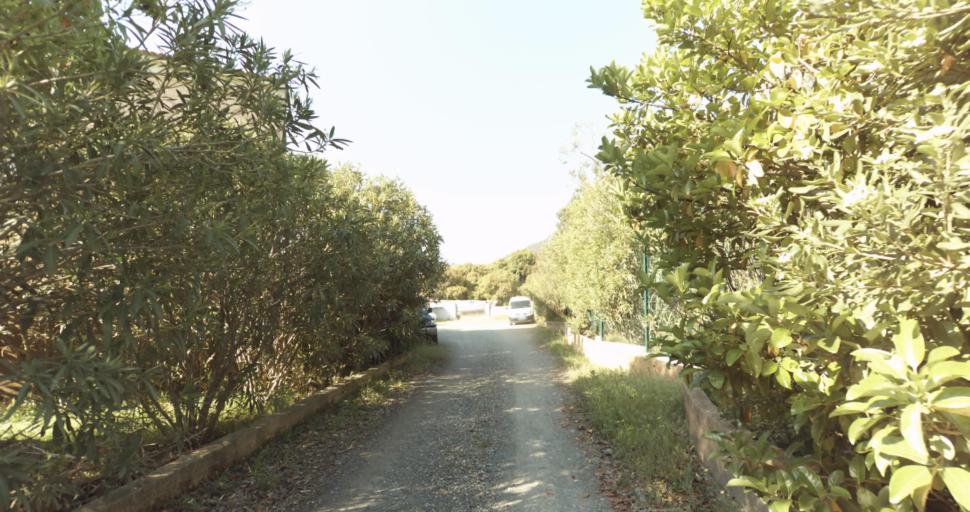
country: FR
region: Corsica
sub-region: Departement de la Haute-Corse
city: Biguglia
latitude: 42.6348
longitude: 9.4293
